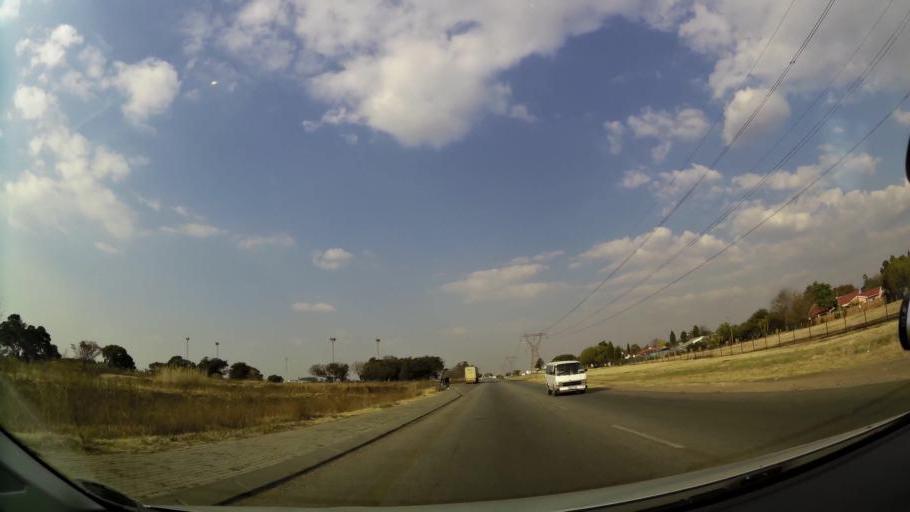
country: ZA
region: Gauteng
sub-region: City of Johannesburg Metropolitan Municipality
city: Modderfontein
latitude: -26.1090
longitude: 28.2038
